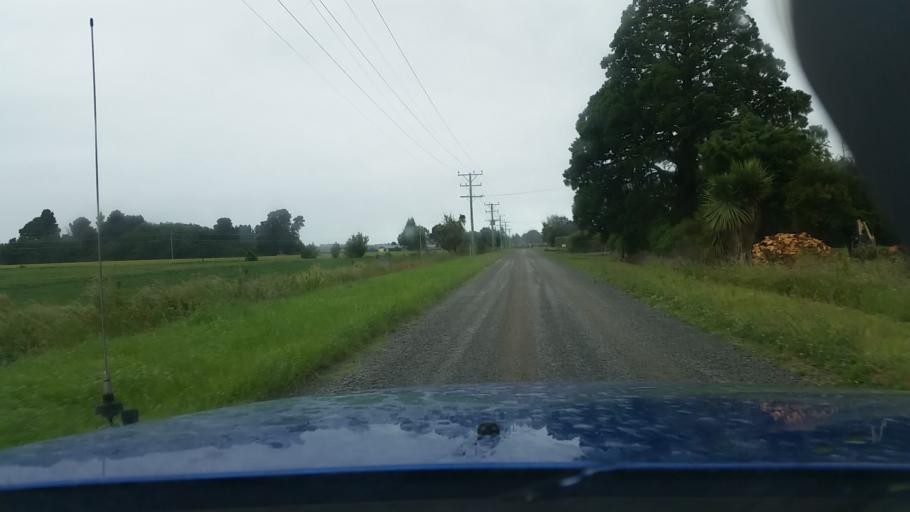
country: NZ
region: Canterbury
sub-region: Ashburton District
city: Tinwald
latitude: -44.0036
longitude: 171.6795
